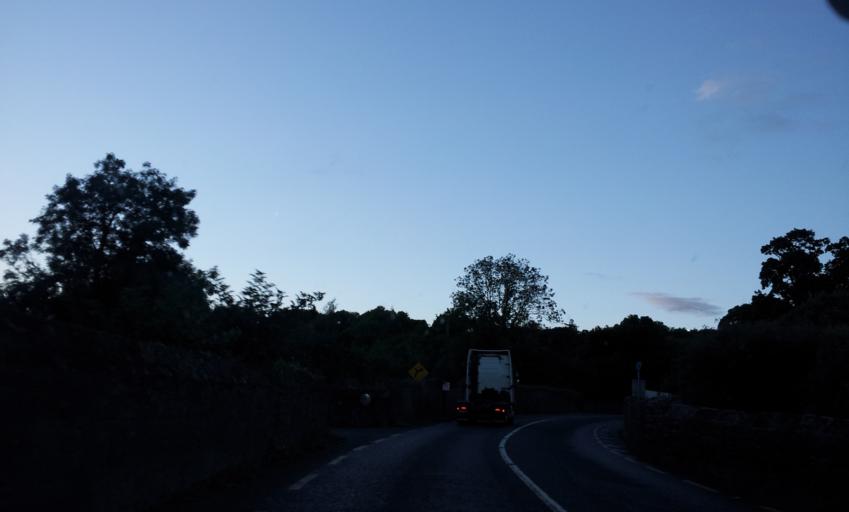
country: IE
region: Munster
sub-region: County Limerick
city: Adare
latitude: 52.5690
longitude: -8.7843
